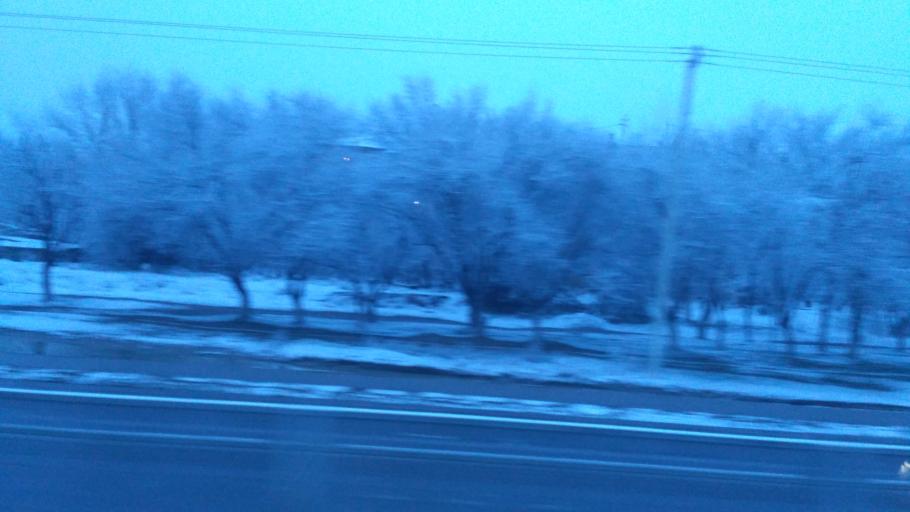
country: KZ
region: Ongtustik Qazaqstan
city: Shymkent
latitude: 42.3802
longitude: 69.4936
